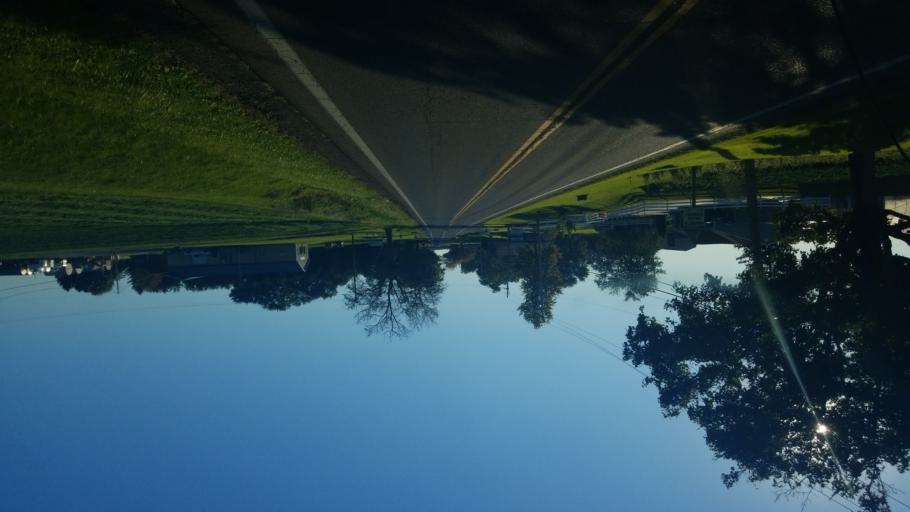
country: US
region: Ohio
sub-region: Columbiana County
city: Leetonia
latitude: 40.9005
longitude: -80.7441
